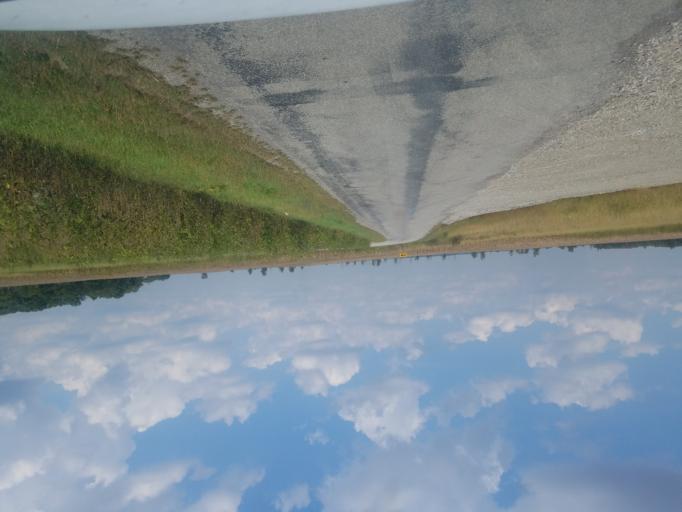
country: US
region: Ohio
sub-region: Hardin County
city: Ada
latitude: 40.6328
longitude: -83.7890
